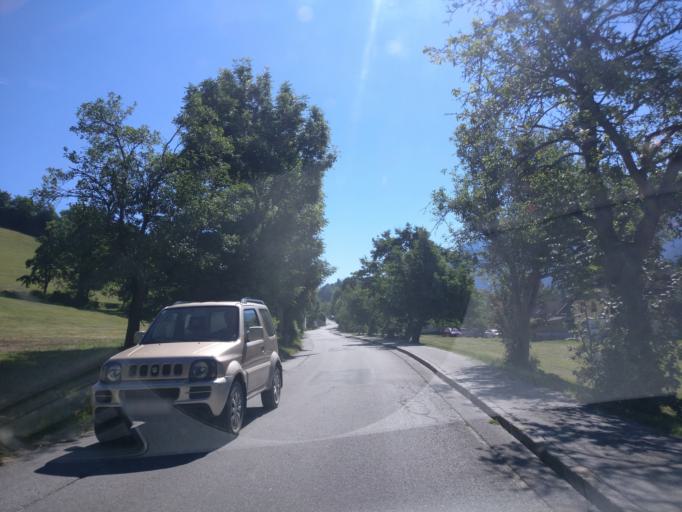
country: AT
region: Salzburg
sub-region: Politischer Bezirk Sankt Johann im Pongau
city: Goldegg
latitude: 47.3158
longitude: 13.0894
